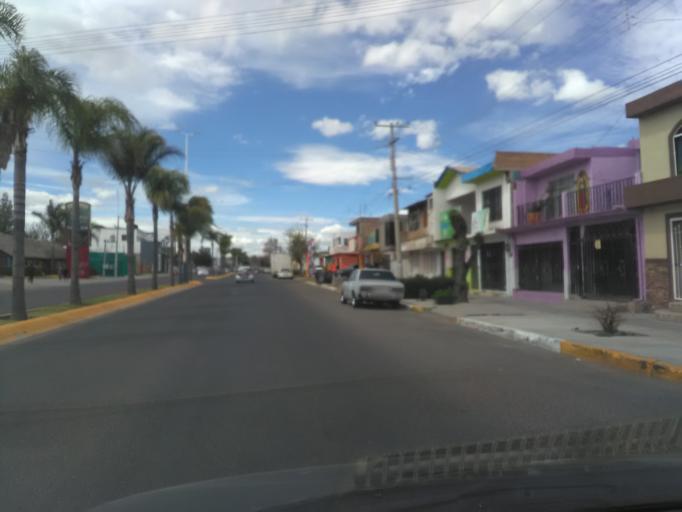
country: MX
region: Durango
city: Victoria de Durango
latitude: 24.0389
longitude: -104.6679
